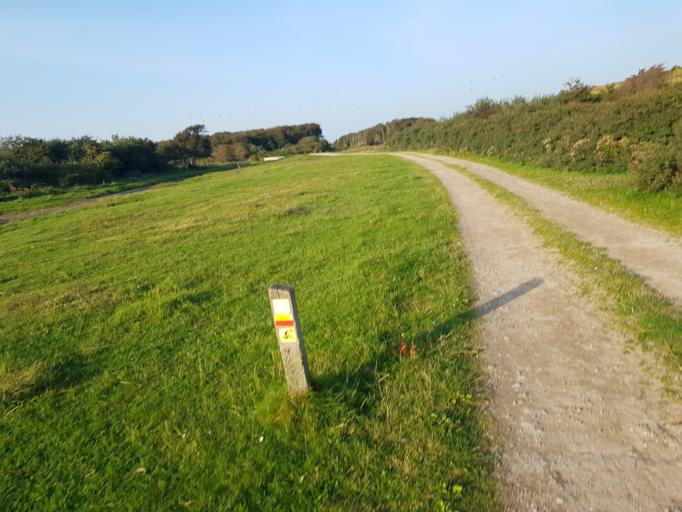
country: NL
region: North Holland
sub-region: Gemeente Texel
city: Den Burg
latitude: 53.1250
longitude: 4.8068
